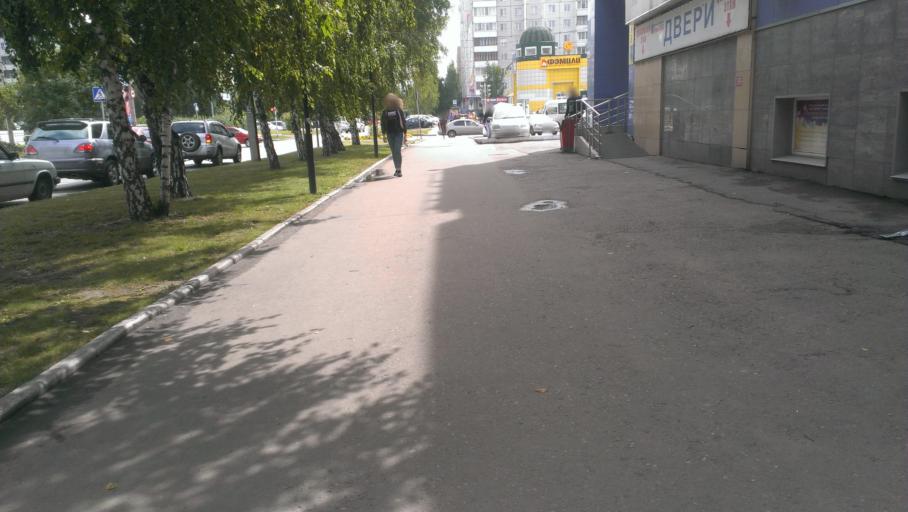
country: RU
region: Altai Krai
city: Novosilikatnyy
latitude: 53.3359
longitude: 83.6770
